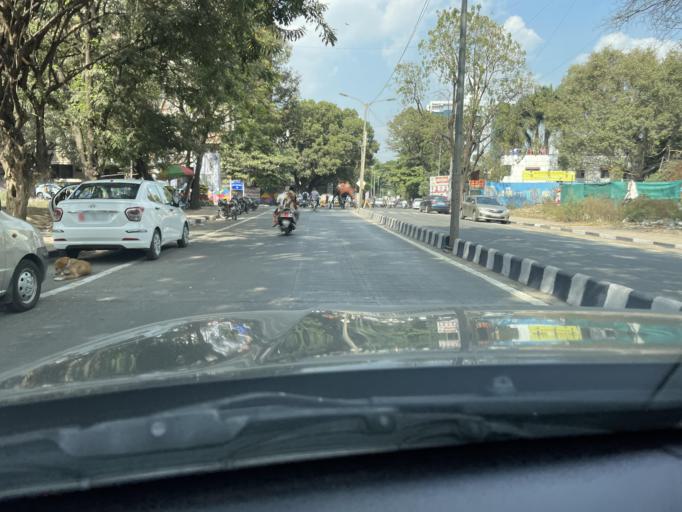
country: IN
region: Maharashtra
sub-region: Pune Division
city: Pune
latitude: 18.4891
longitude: 73.9000
